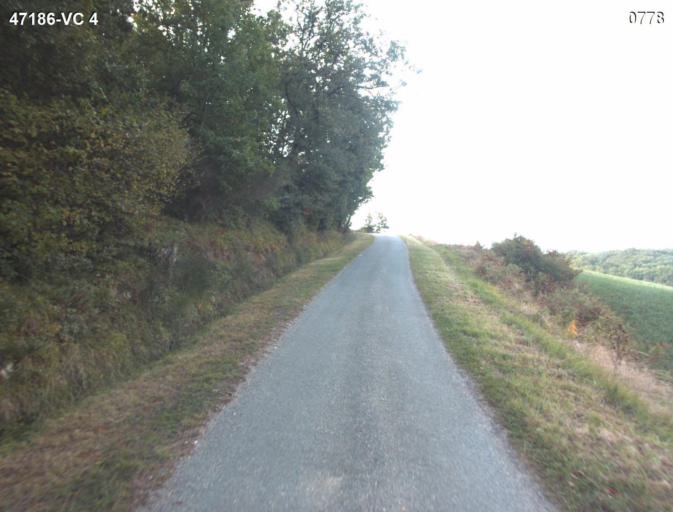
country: FR
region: Aquitaine
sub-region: Departement du Lot-et-Garonne
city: Port-Sainte-Marie
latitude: 44.2005
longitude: 0.4263
